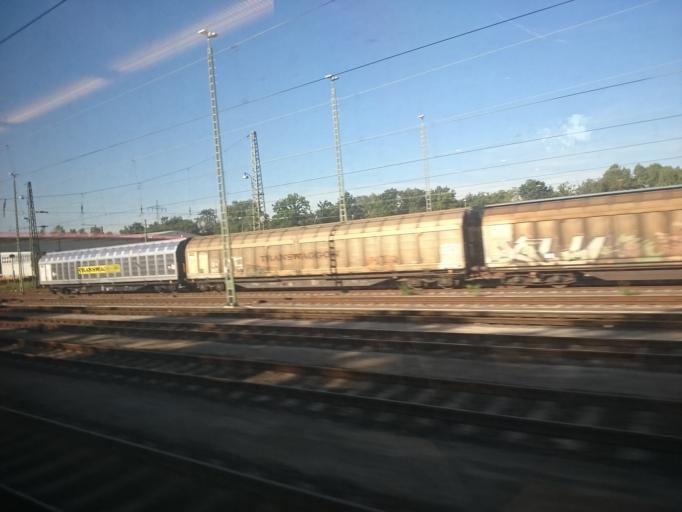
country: DE
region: North Rhine-Westphalia
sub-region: Regierungsbezirk Dusseldorf
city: Hochfeld
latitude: 51.3785
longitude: 6.8133
